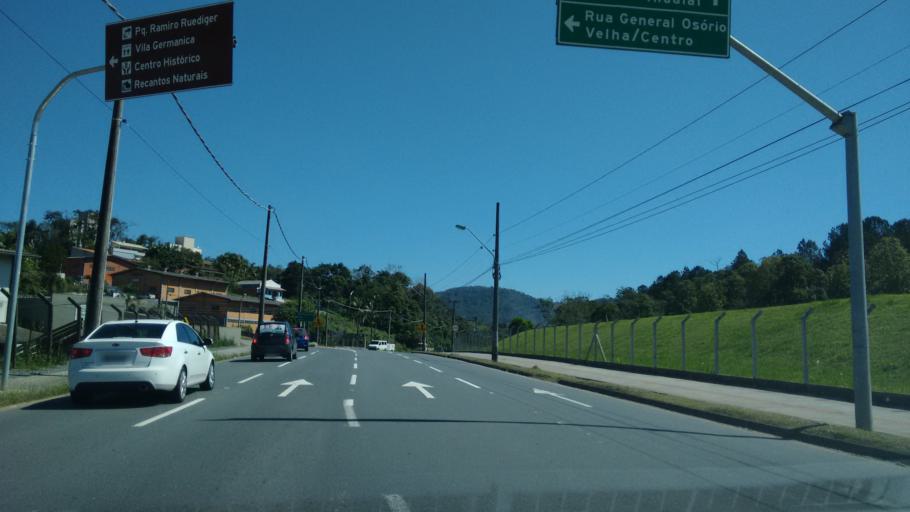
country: BR
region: Santa Catarina
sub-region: Blumenau
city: Blumenau
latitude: -26.8983
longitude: -49.1364
